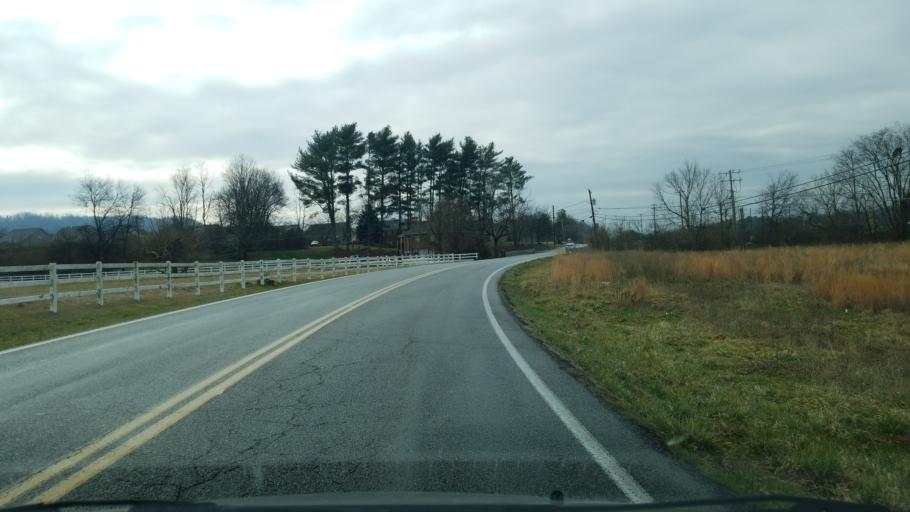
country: US
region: Tennessee
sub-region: Hamilton County
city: East Brainerd
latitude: 35.0075
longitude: -85.0908
